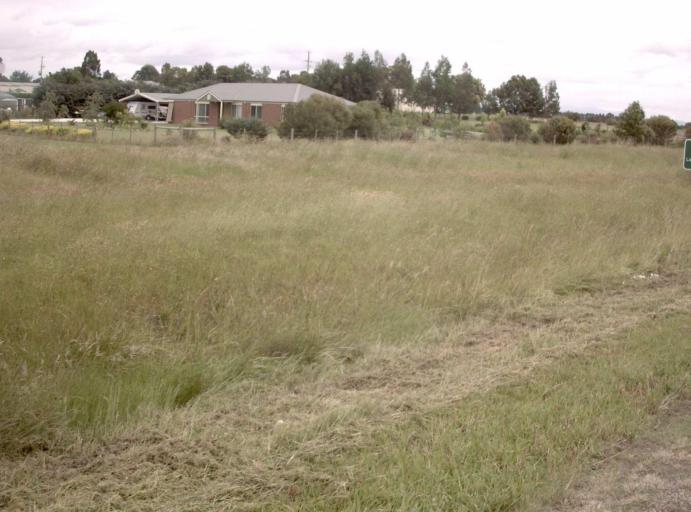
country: AU
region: Victoria
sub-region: Wellington
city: Sale
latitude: -37.9566
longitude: 147.0847
